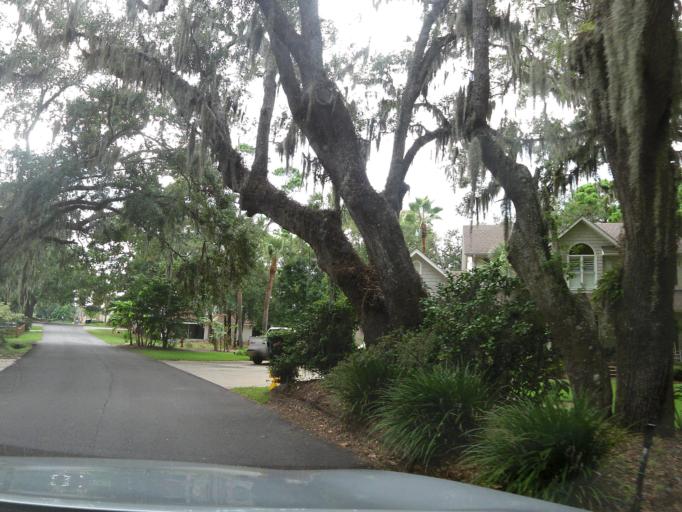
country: US
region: Georgia
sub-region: Glynn County
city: Saint Simons Island
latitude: 31.1601
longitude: -81.3863
